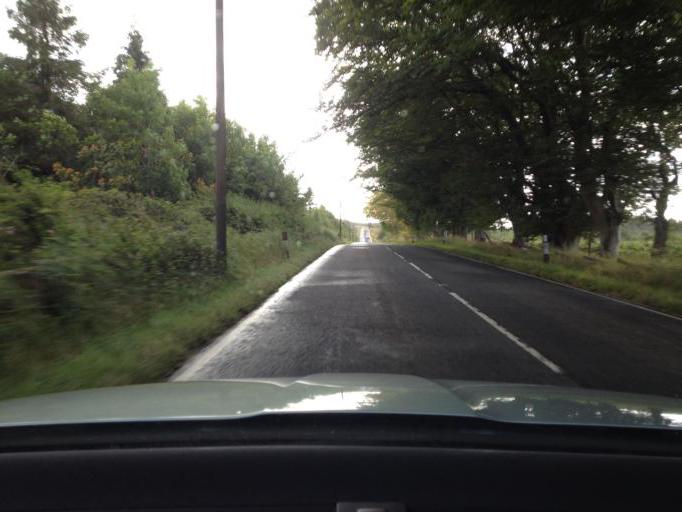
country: GB
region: Scotland
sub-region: West Lothian
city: West Calder
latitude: 55.8228
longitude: -3.5285
